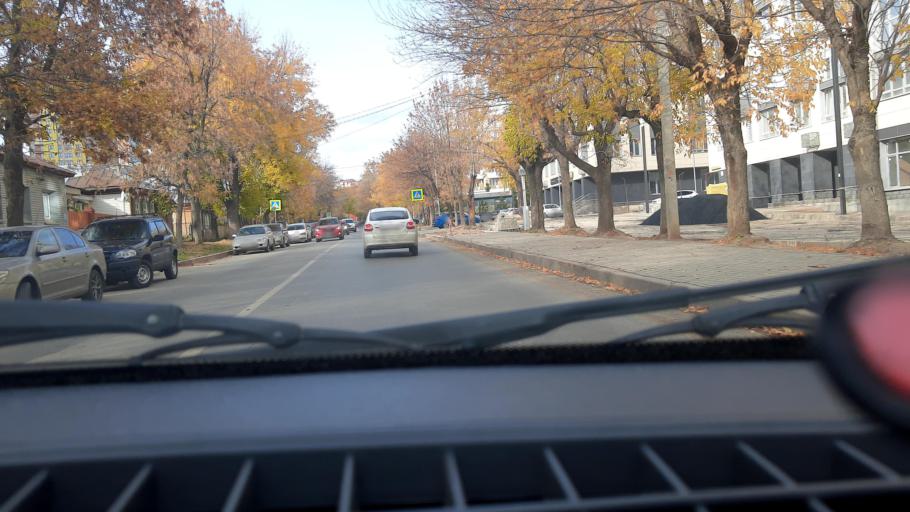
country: RU
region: Bashkortostan
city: Ufa
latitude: 54.7196
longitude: 55.9625
